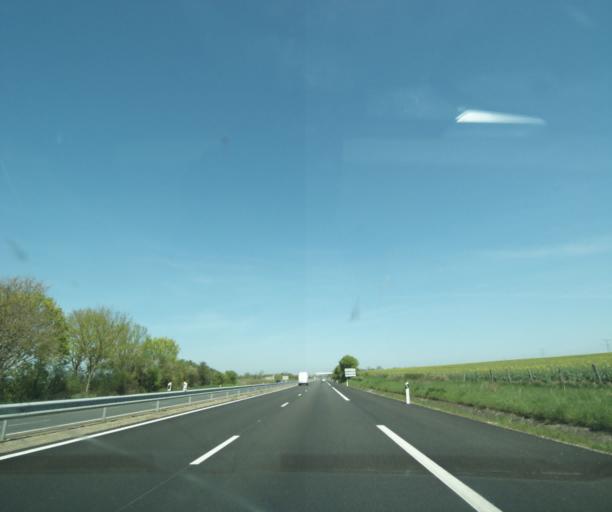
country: FR
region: Bourgogne
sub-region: Departement de la Nievre
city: La Charite-sur-Loire
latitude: 47.1443
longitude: 3.0455
